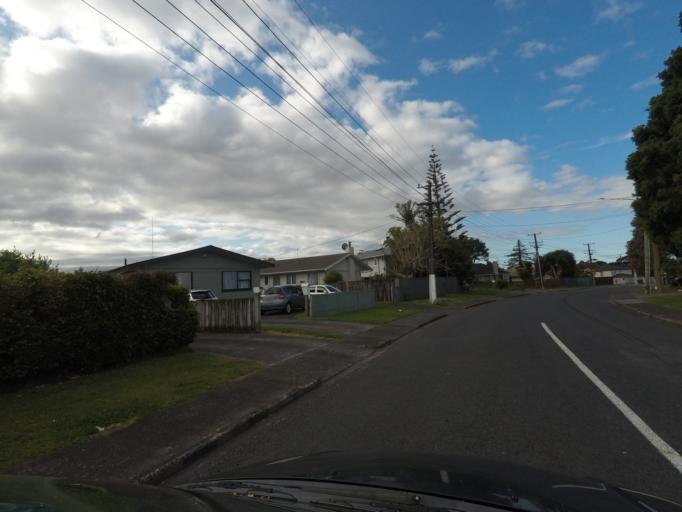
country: NZ
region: Auckland
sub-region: Auckland
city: Rosebank
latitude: -36.8847
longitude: 174.6562
